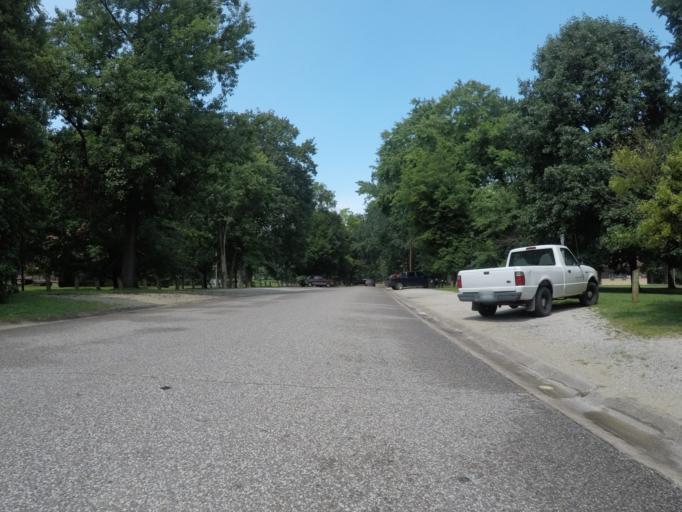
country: US
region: Kentucky
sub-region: Boyd County
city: Ashland
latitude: 38.4723
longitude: -82.6355
